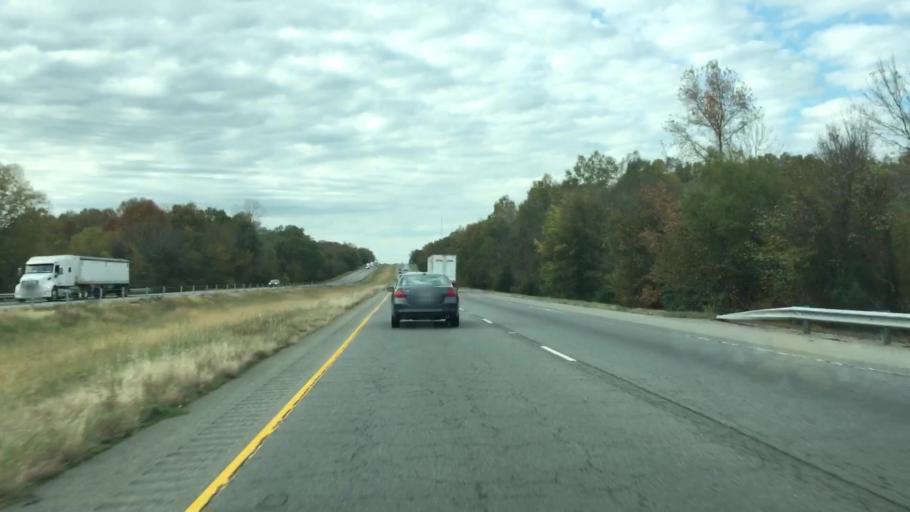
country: US
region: Arkansas
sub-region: Faulkner County
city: Conway
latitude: 35.1396
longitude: -92.5248
